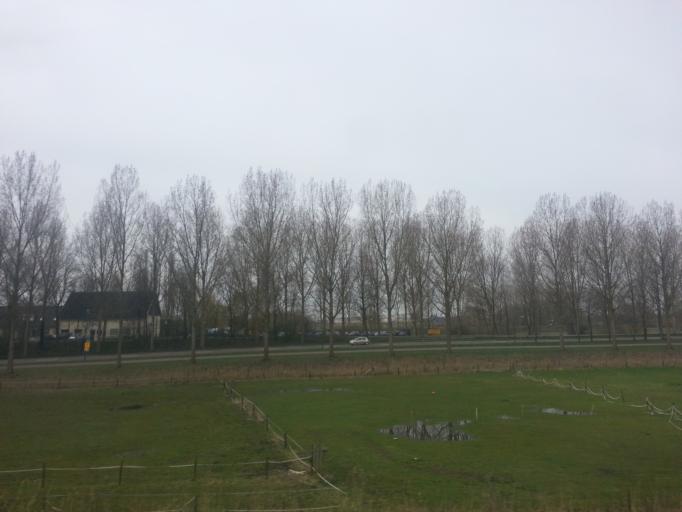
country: NL
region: North Brabant
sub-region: Gemeente 's-Hertogenbosch
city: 's-Hertogenbosch
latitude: 51.7133
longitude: 5.2932
